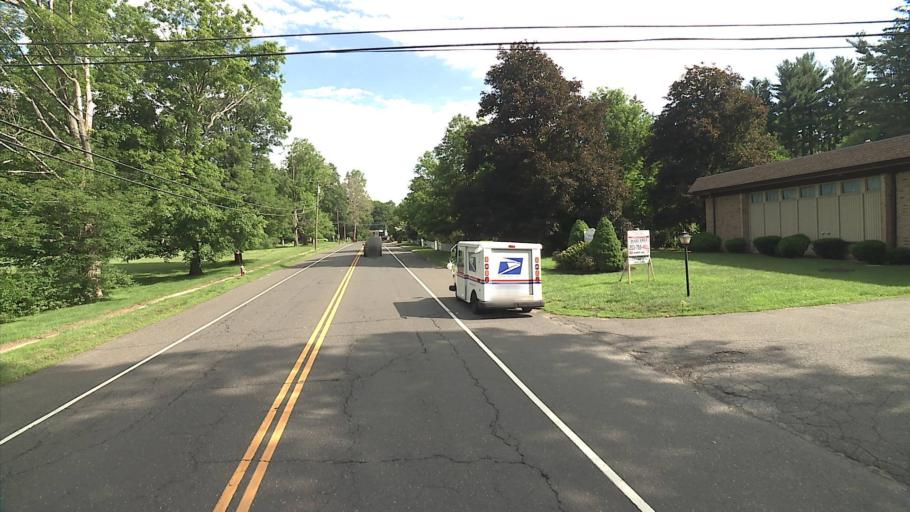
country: US
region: Connecticut
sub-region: New Haven County
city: Naugatuck
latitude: 41.5027
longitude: -73.0586
